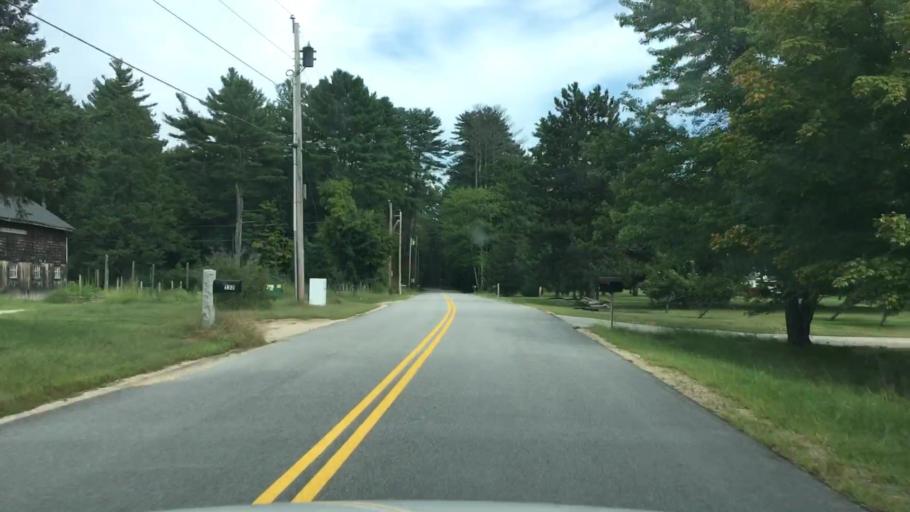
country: US
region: New Hampshire
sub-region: Strafford County
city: Barrington
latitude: 43.2012
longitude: -70.9838
